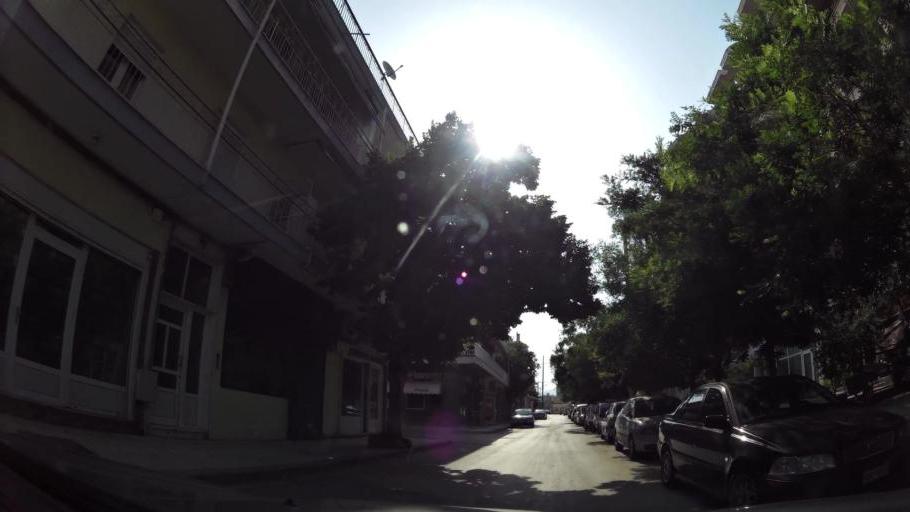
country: GR
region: Central Macedonia
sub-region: Nomos Thessalonikis
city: Ampelokipoi
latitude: 40.6651
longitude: 22.9219
